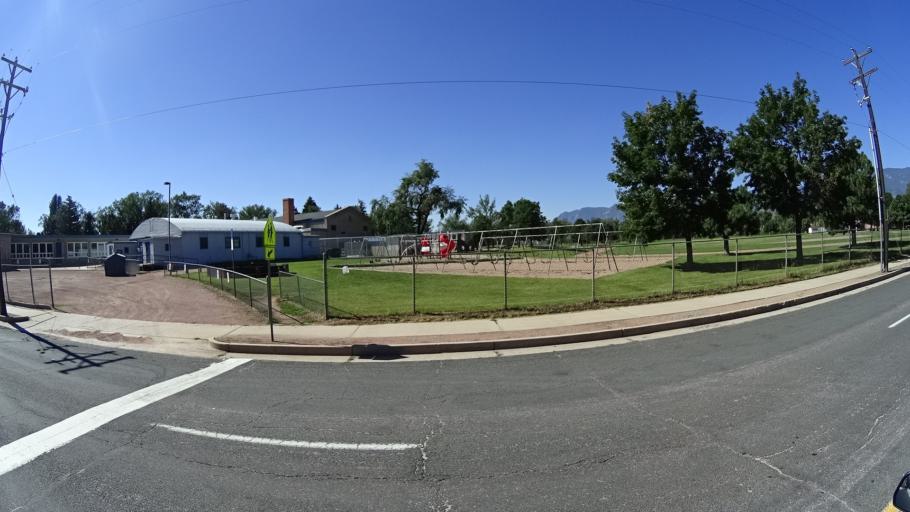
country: US
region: Colorado
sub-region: El Paso County
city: Colorado Springs
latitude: 38.8755
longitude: -104.7821
